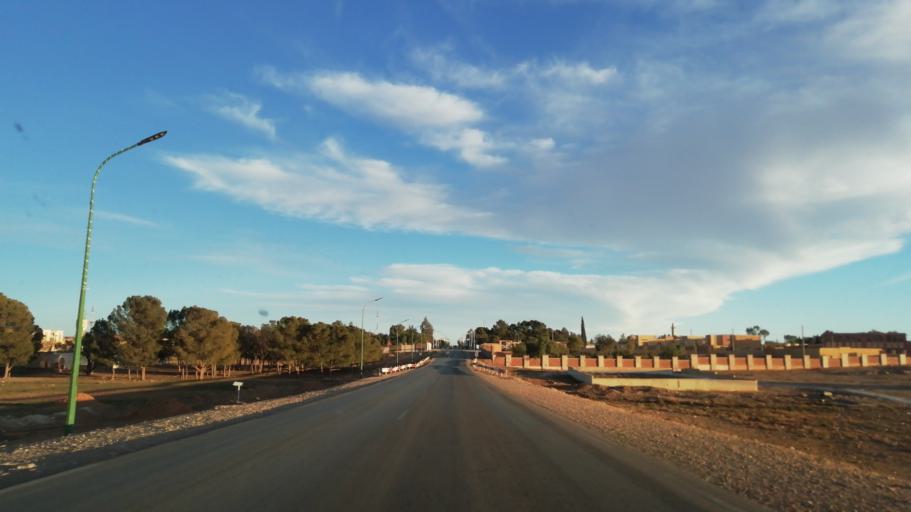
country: DZ
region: Wilaya de Naama
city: Naama
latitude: 33.7210
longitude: -0.7346
